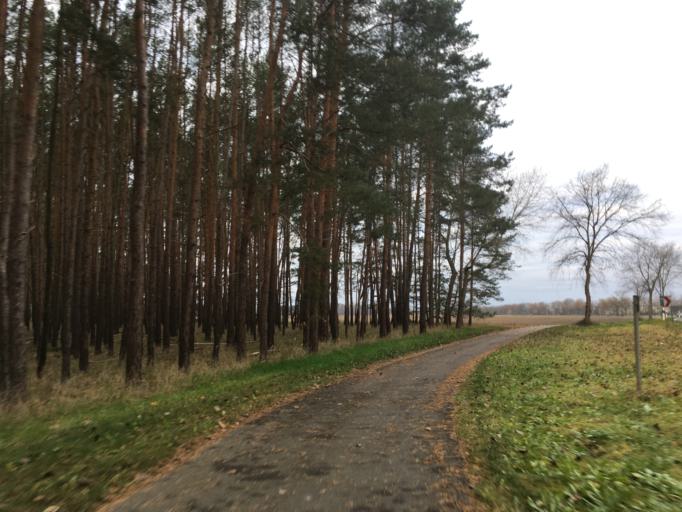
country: DE
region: Brandenburg
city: Neuhardenberg
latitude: 52.5853
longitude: 14.2947
